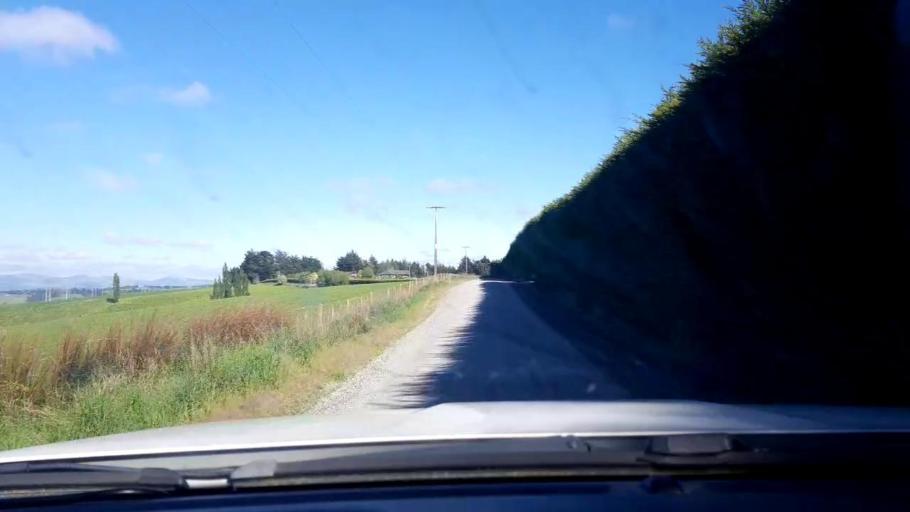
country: NZ
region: Otago
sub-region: Clutha District
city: Balclutha
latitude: -46.2239
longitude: 169.7645
